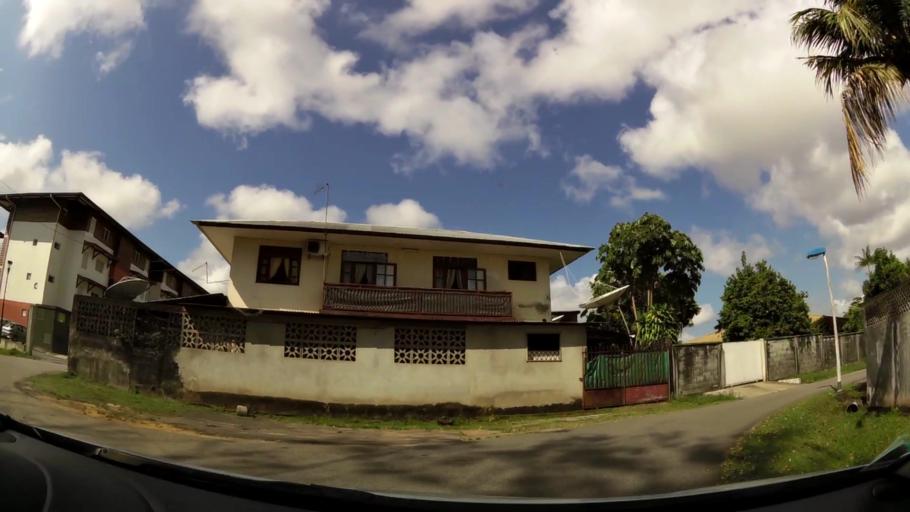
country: GF
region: Guyane
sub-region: Guyane
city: Cayenne
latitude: 4.9316
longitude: -52.3149
